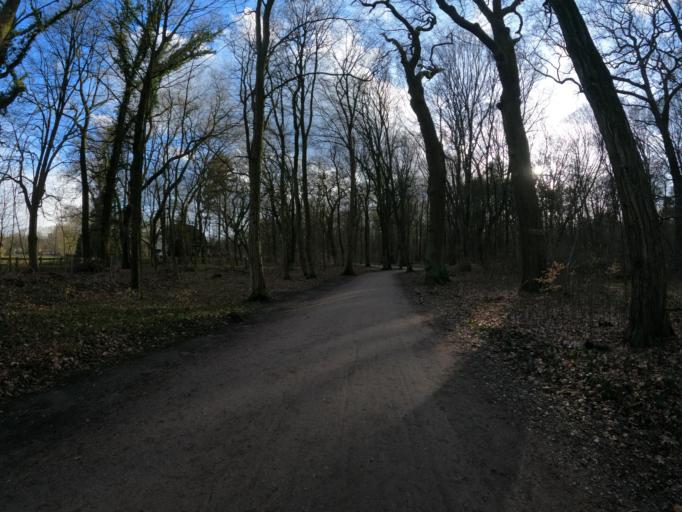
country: DE
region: Hamburg
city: Stellingen
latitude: 53.6112
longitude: 9.9396
